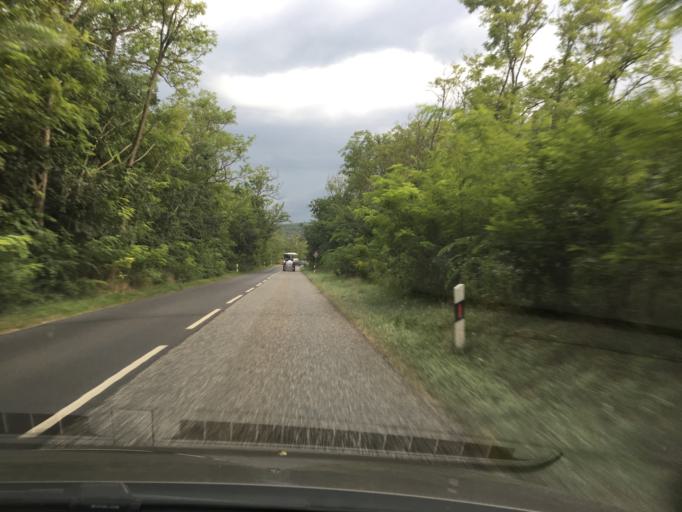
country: HU
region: Pest
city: Szada
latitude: 47.6114
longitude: 19.2977
